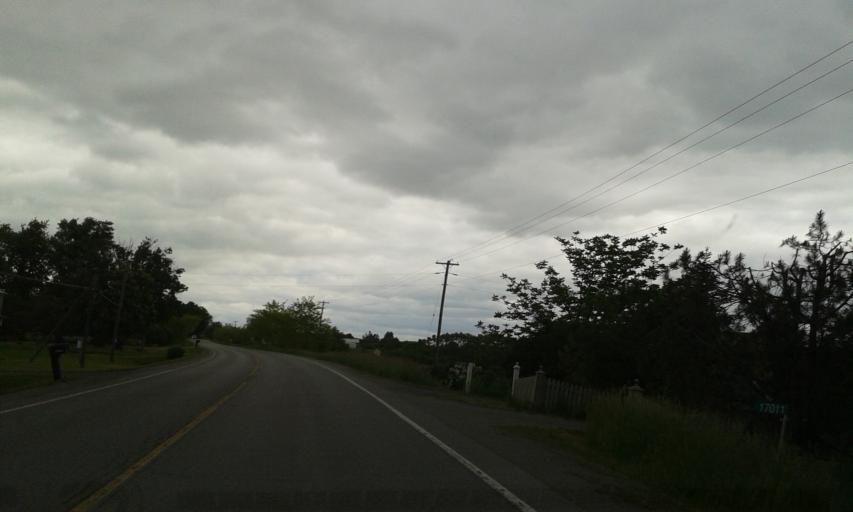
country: CA
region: Ontario
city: Prince Edward
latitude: 43.9429
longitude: -77.3802
